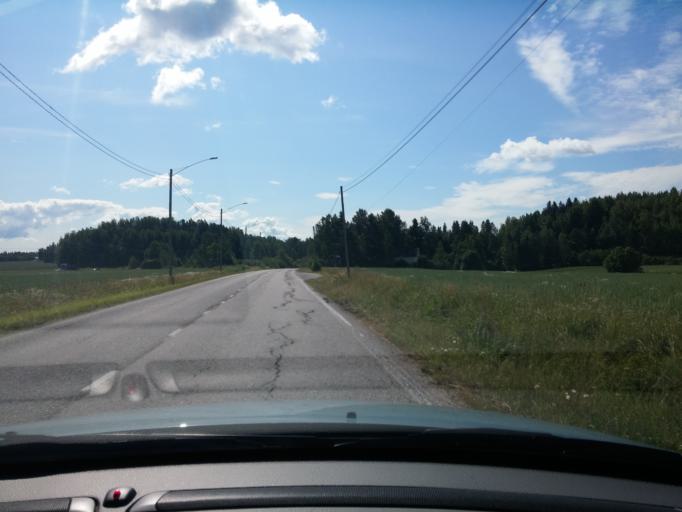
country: FI
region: Uusimaa
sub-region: Porvoo
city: Askola
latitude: 60.4551
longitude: 25.5785
